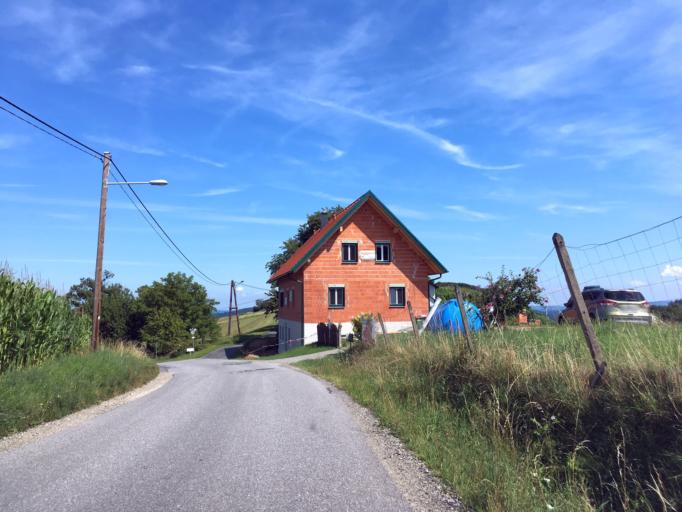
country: AT
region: Styria
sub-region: Politischer Bezirk Leibnitz
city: Sankt Nikolai im Sausal
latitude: 46.8045
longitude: 15.4408
